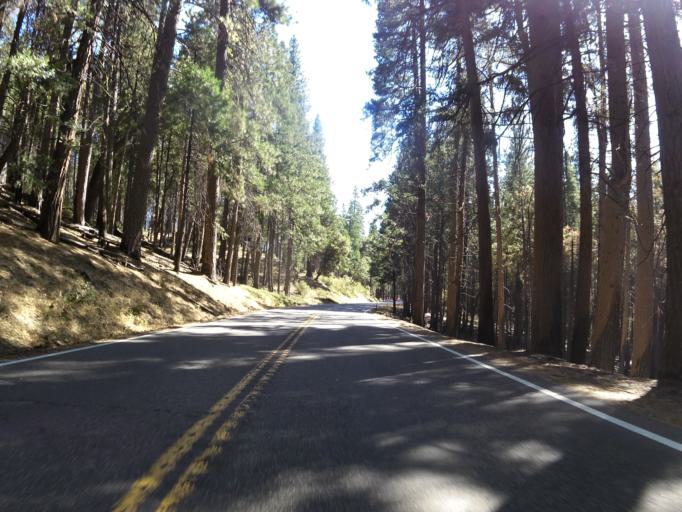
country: US
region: California
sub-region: Madera County
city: Ahwahnee
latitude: 37.5655
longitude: -119.6926
